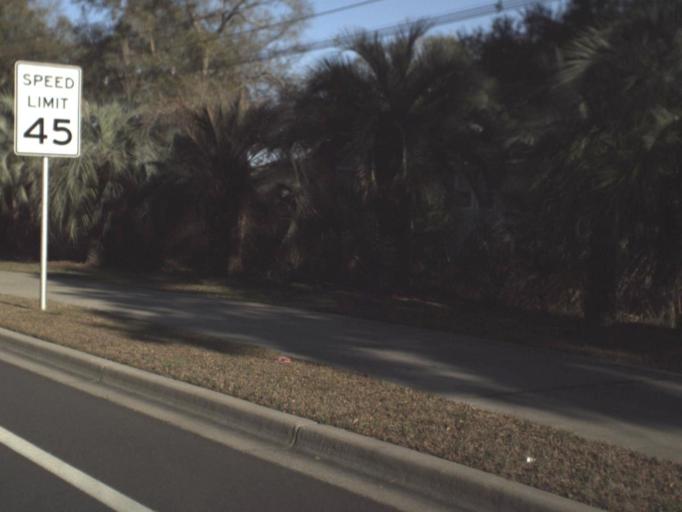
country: US
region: Florida
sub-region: Leon County
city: Tallahassee
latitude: 30.4675
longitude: -84.2071
